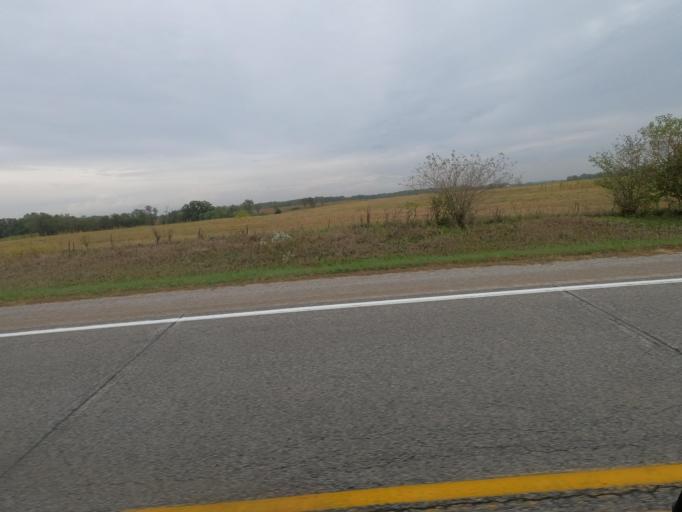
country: US
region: Iowa
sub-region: Van Buren County
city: Keosauqua
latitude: 40.8502
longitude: -92.0369
